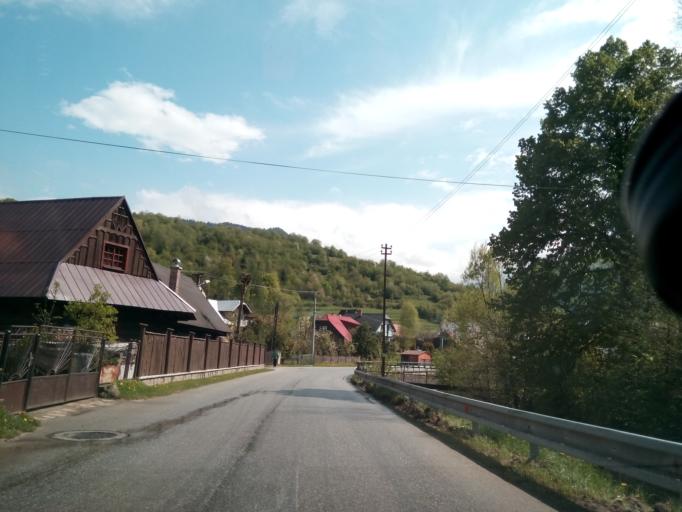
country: SK
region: Zilinsky
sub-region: Okres Zilina
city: Terchova
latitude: 49.2653
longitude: 19.0334
